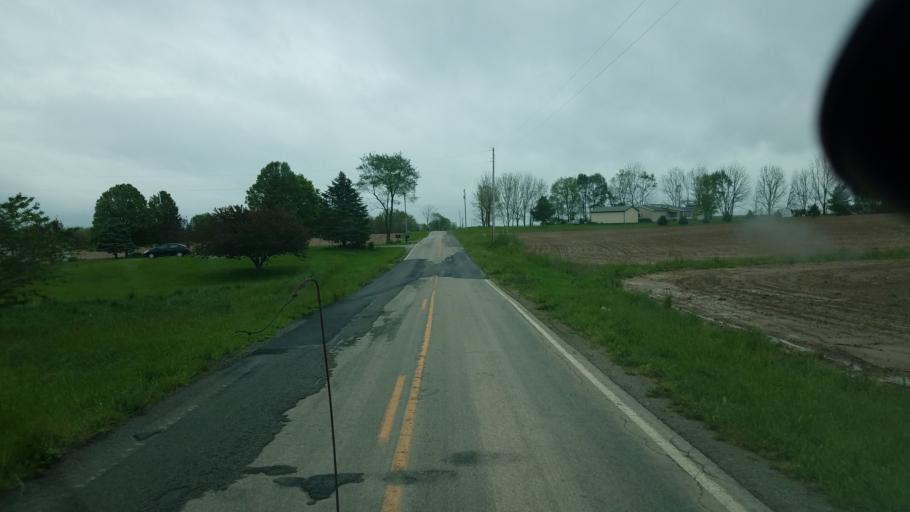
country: US
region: Ohio
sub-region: Highland County
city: Leesburg
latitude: 39.3305
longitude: -83.4958
